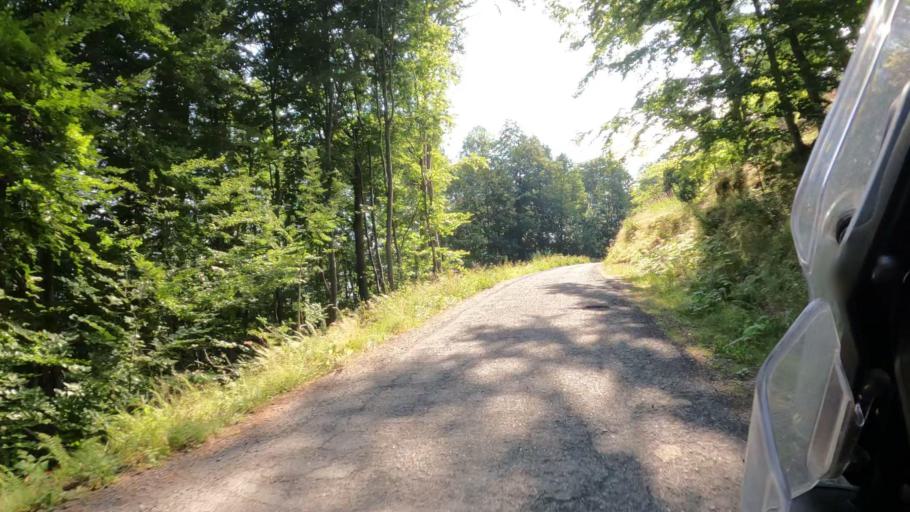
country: IT
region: Piedmont
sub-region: Provincia di Torino
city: Lemie
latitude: 45.2178
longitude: 7.3123
